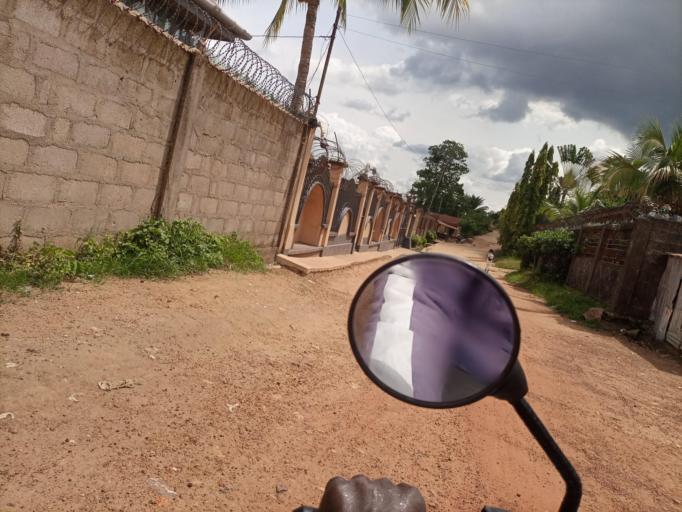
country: SL
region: Southern Province
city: Bo
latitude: 7.9500
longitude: -11.7372
